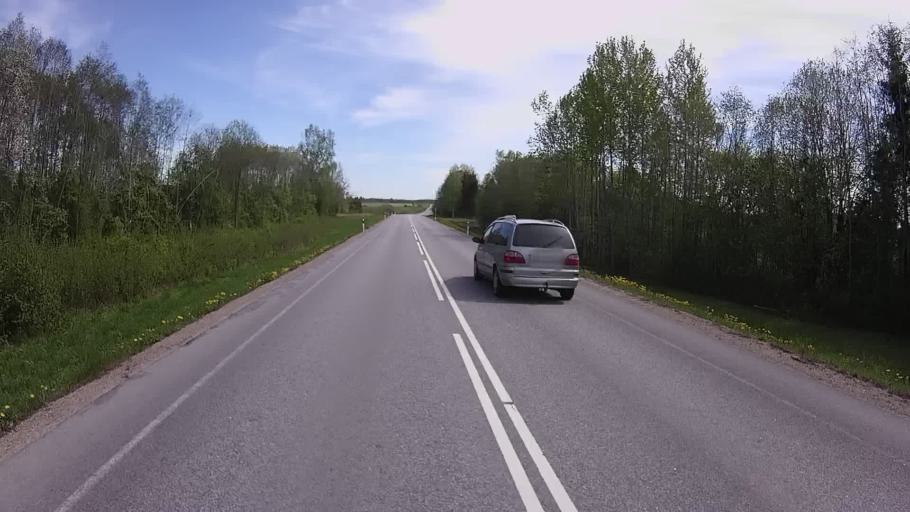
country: EE
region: Valgamaa
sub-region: Valga linn
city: Valga
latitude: 57.7287
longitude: 26.1756
